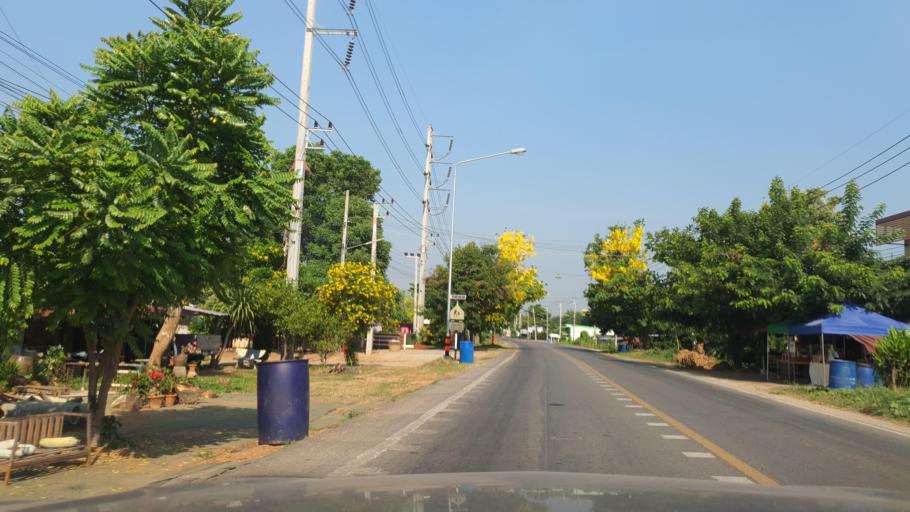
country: TH
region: Kanchanaburi
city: Kanchanaburi
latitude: 14.0355
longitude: 99.4942
